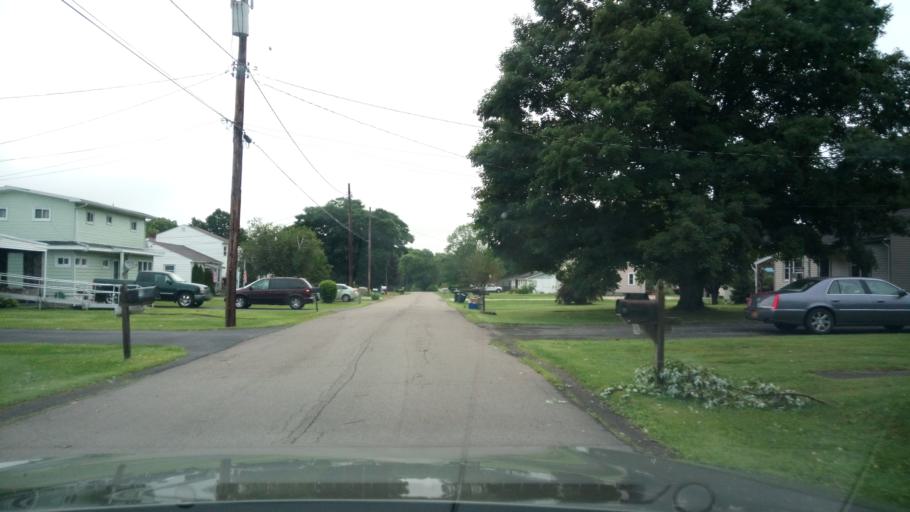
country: US
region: New York
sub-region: Chemung County
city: West Elmira
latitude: 42.0826
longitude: -76.8773
